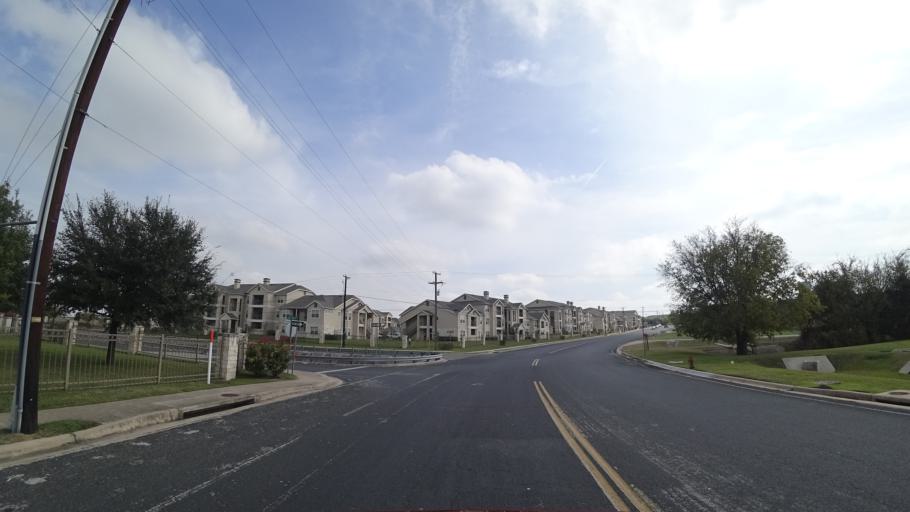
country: US
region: Texas
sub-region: Travis County
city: Windemere
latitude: 30.4543
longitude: -97.6562
